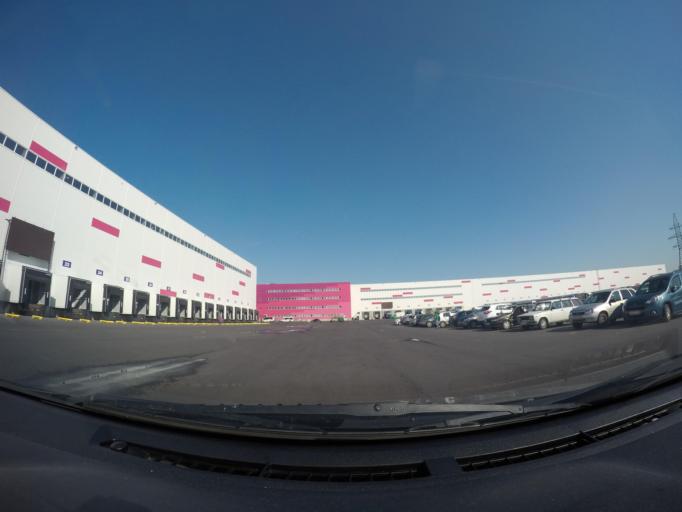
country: RU
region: Moskovskaya
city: Fryazevo
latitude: 55.7444
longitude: 38.4213
